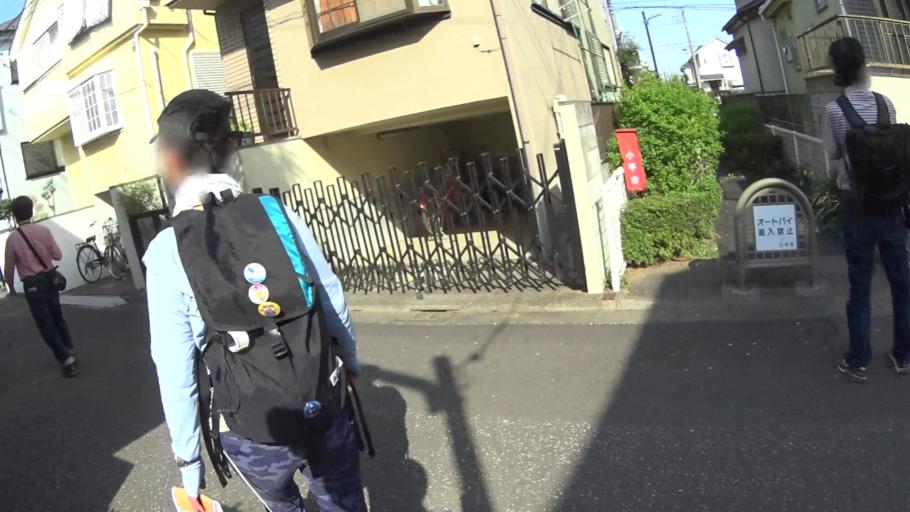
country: JP
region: Tokyo
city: Kokubunji
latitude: 35.7173
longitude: 139.4930
